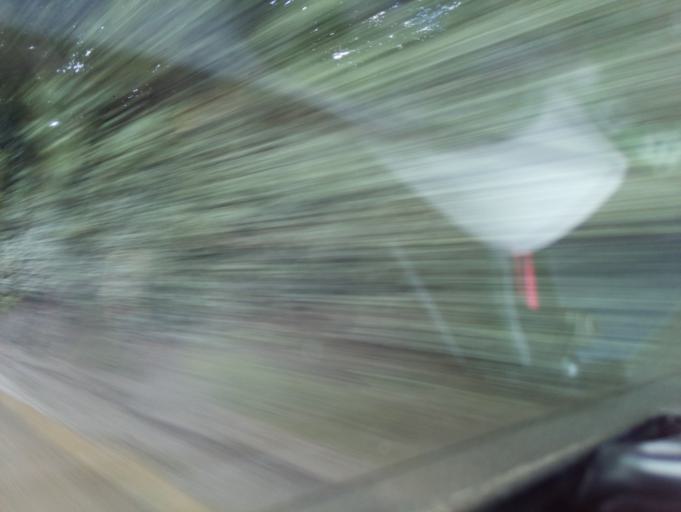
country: GB
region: England
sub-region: Devon
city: Modbury
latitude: 50.3328
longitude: -3.8481
